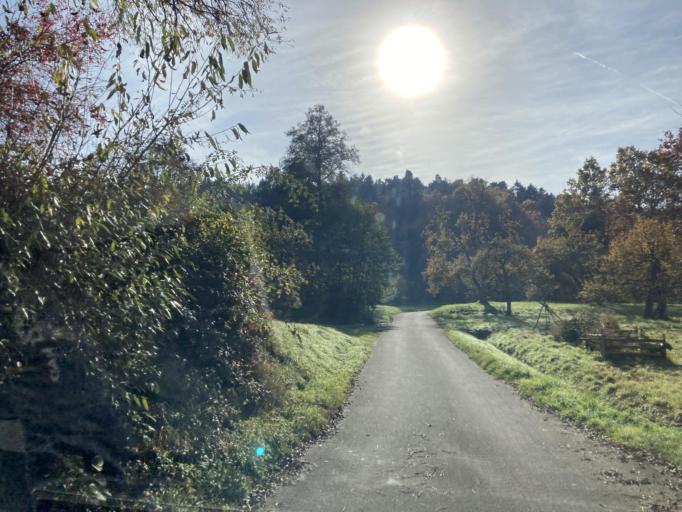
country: DE
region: Baden-Wuerttemberg
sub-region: Tuebingen Region
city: Rottenburg
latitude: 48.4669
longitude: 8.9794
